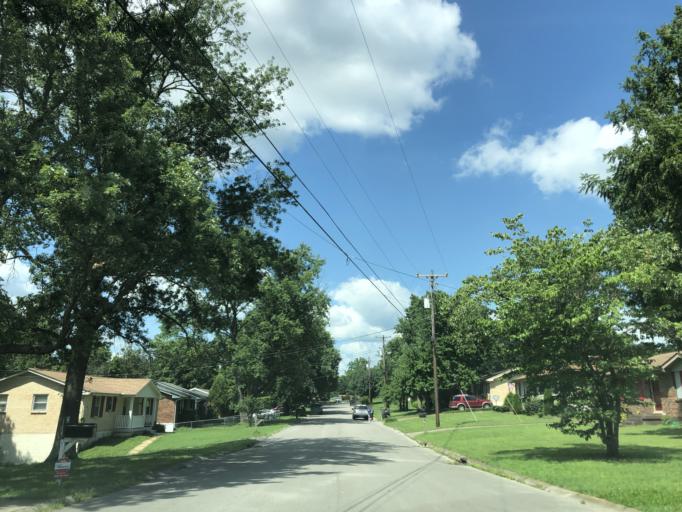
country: US
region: Tennessee
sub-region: Wilson County
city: Green Hill
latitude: 36.2222
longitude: -86.5884
